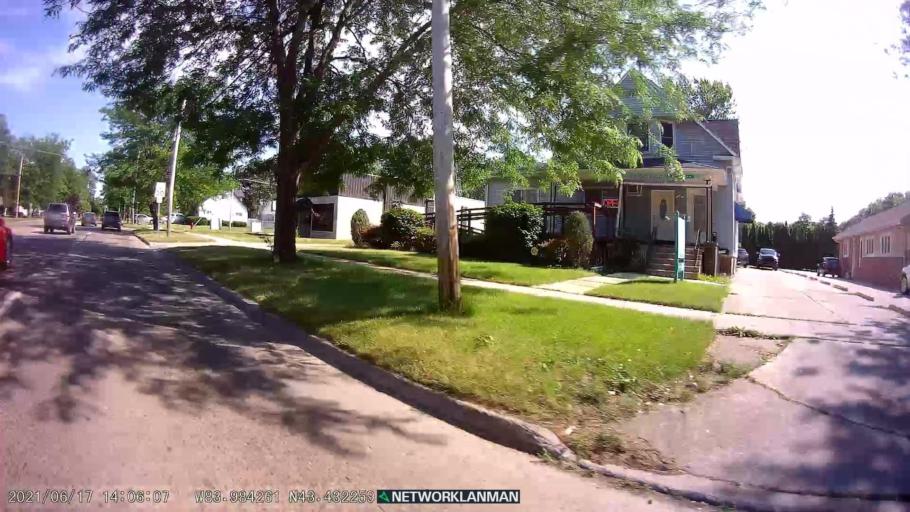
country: US
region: Michigan
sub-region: Saginaw County
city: Saginaw
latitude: 43.4322
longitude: -83.9842
